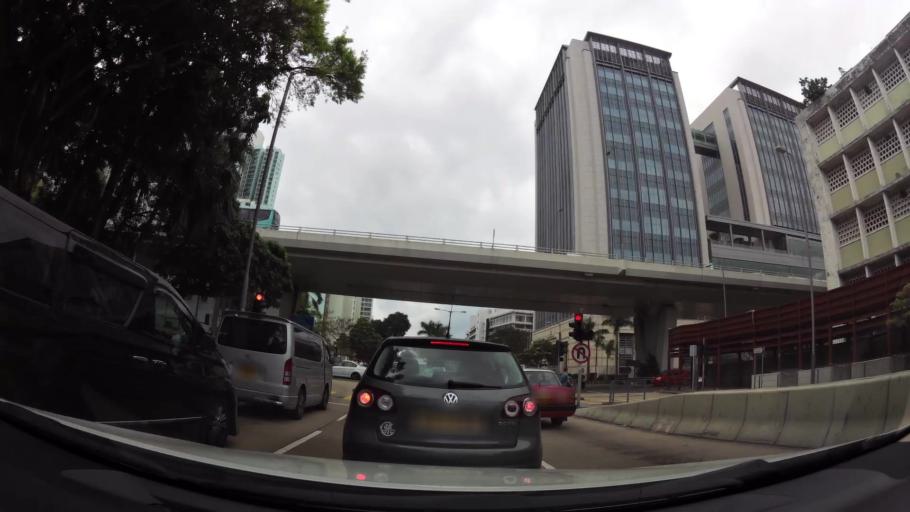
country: HK
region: Sham Shui Po
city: Sham Shui Po
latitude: 22.3312
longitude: 114.1545
